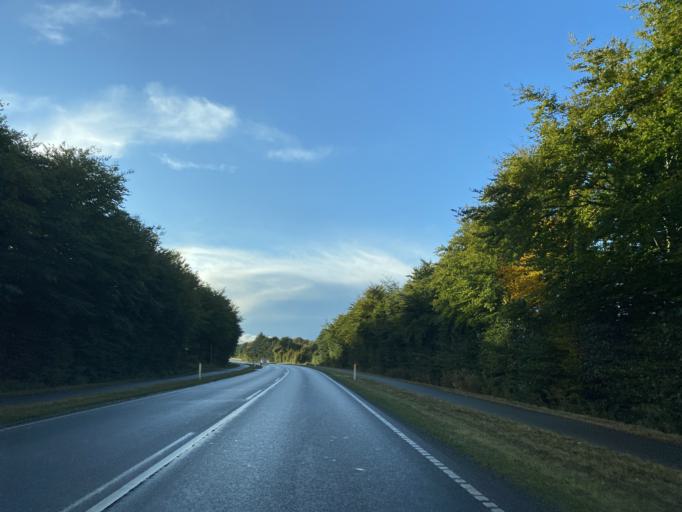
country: DK
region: South Denmark
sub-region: Haderslev Kommune
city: Haderslev
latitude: 55.2465
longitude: 9.4315
